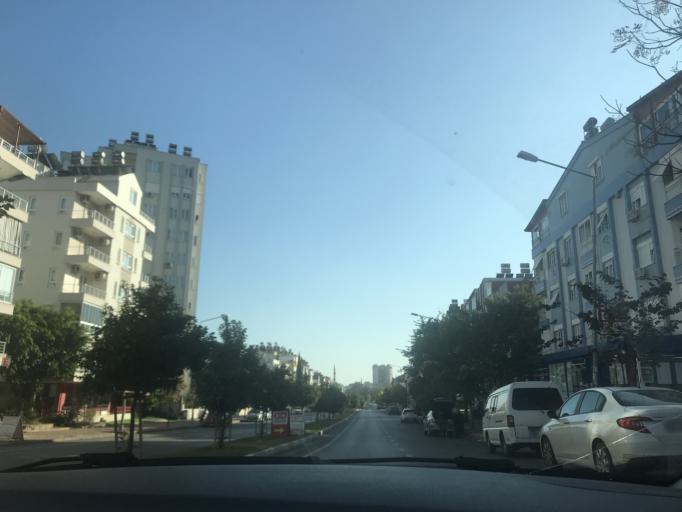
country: TR
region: Antalya
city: Antalya
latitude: 36.8873
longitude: 30.6470
